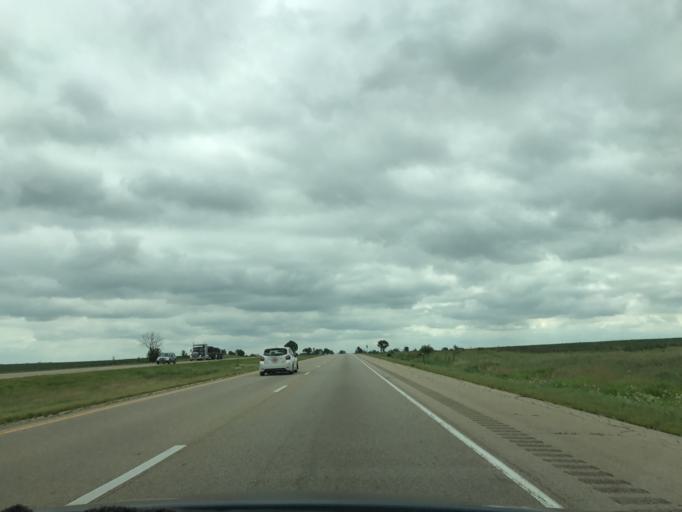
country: US
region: Illinois
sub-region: Bureau County
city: Depue
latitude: 41.3928
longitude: -89.2917
